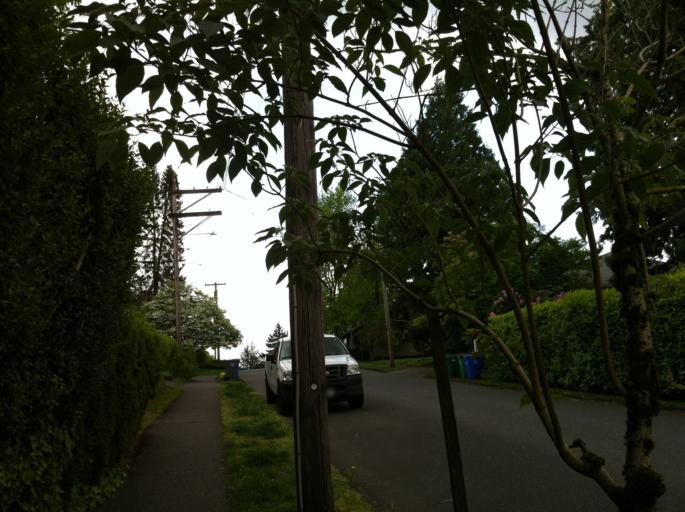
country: US
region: Oregon
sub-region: Clackamas County
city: Lake Oswego
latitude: 45.4655
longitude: -122.6872
